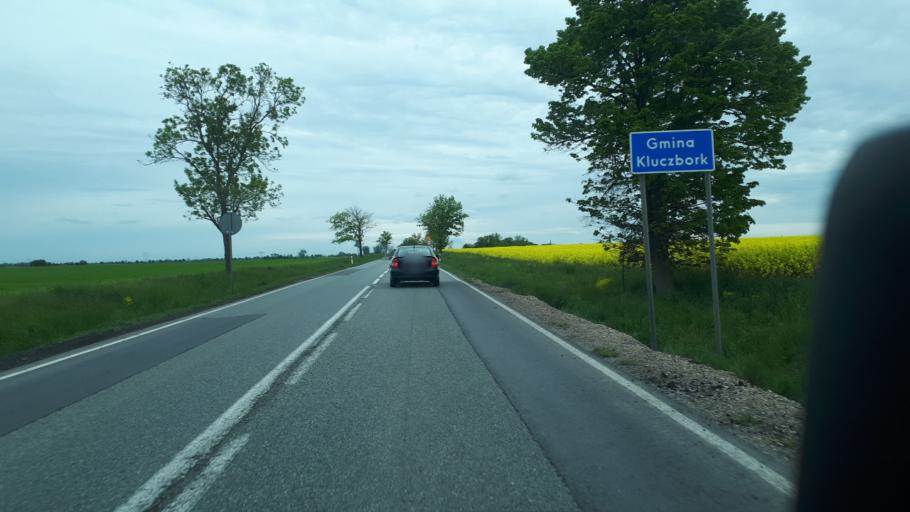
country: PL
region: Opole Voivodeship
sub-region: Powiat kluczborski
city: Byczyna
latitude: 51.0506
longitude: 18.1966
